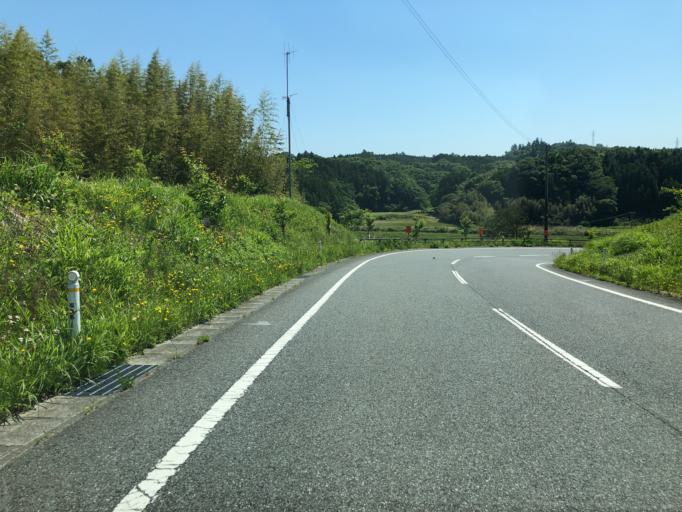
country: JP
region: Fukushima
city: Iwaki
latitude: 37.2334
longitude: 140.9894
